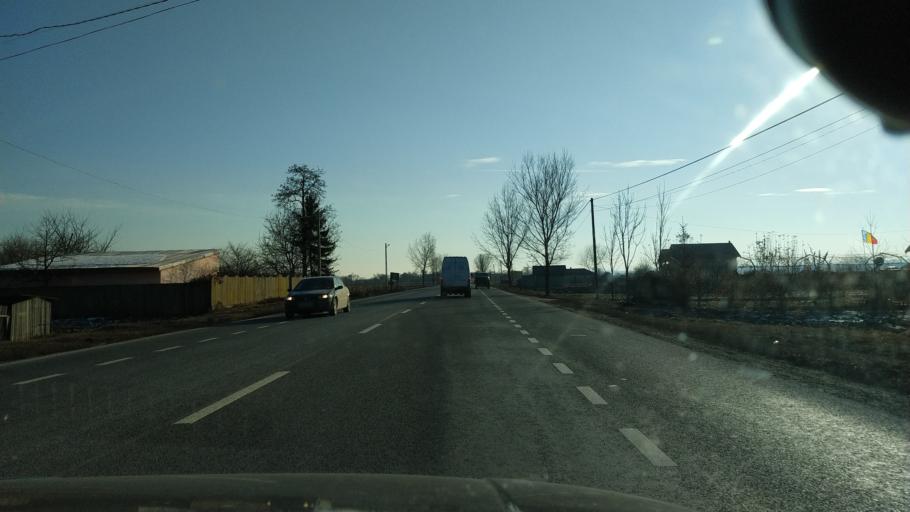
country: RO
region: Neamt
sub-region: Comuna Icusesti
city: Icusesti
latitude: 46.8107
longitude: 26.8864
